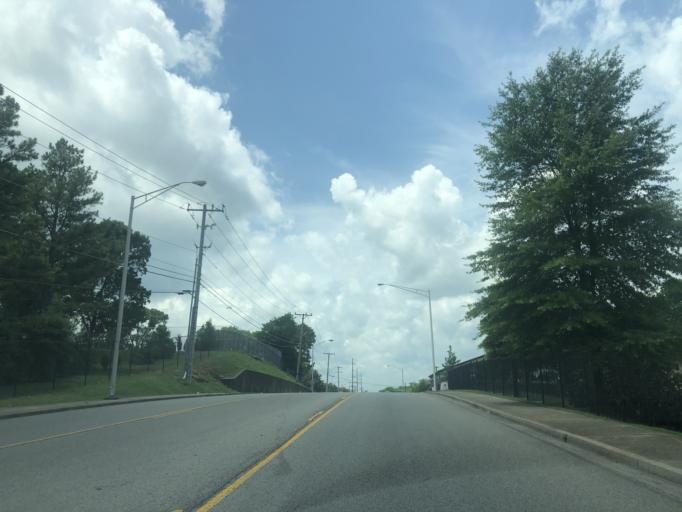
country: US
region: Tennessee
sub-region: Davidson County
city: Nashville
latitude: 36.1876
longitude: -86.8003
